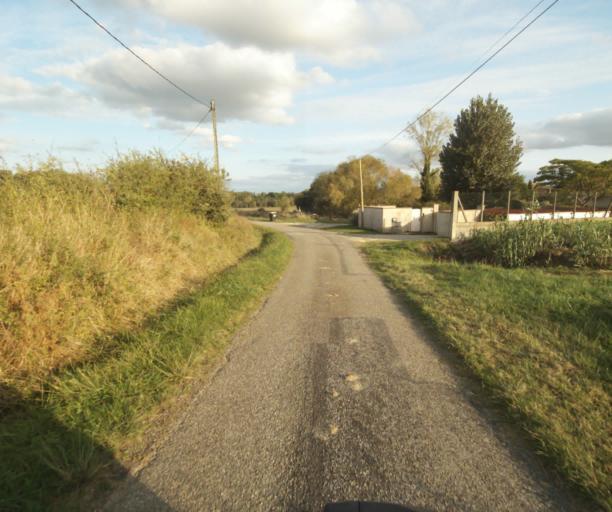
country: FR
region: Midi-Pyrenees
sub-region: Departement de la Haute-Garonne
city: Launac
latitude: 43.8291
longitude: 1.1257
